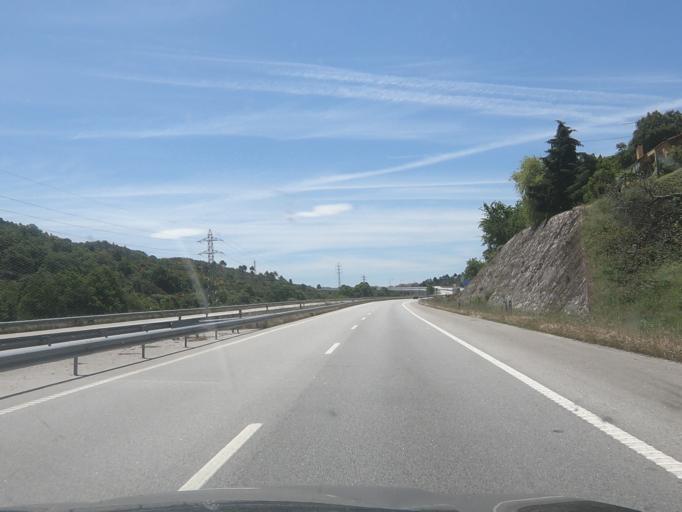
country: PT
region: Guarda
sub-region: Guarda
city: Sequeira
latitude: 40.5762
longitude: -7.2510
